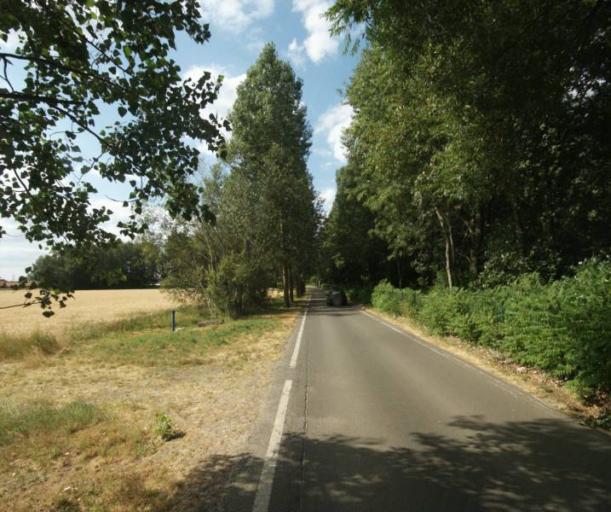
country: FR
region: Nord-Pas-de-Calais
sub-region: Departement du Nord
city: Bondues
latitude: 50.7084
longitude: 3.1104
